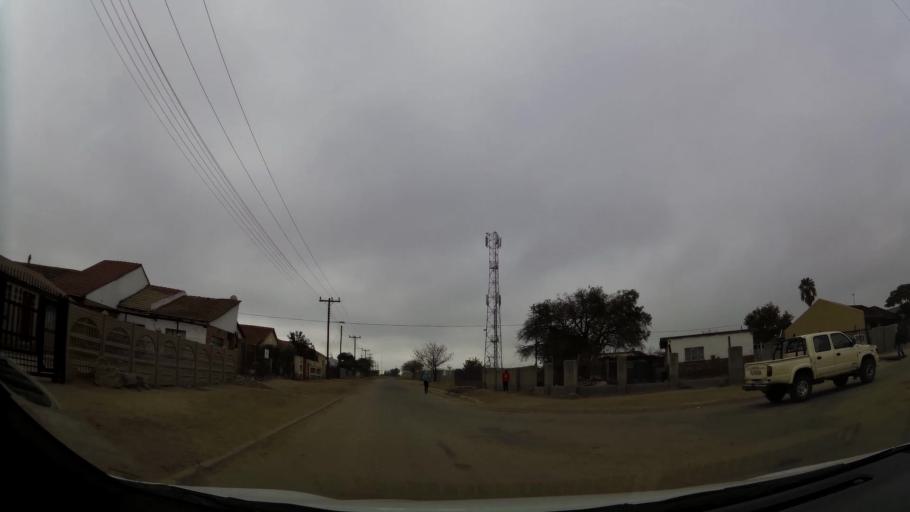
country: ZA
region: Limpopo
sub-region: Capricorn District Municipality
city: Polokwane
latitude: -23.8371
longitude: 29.3929
